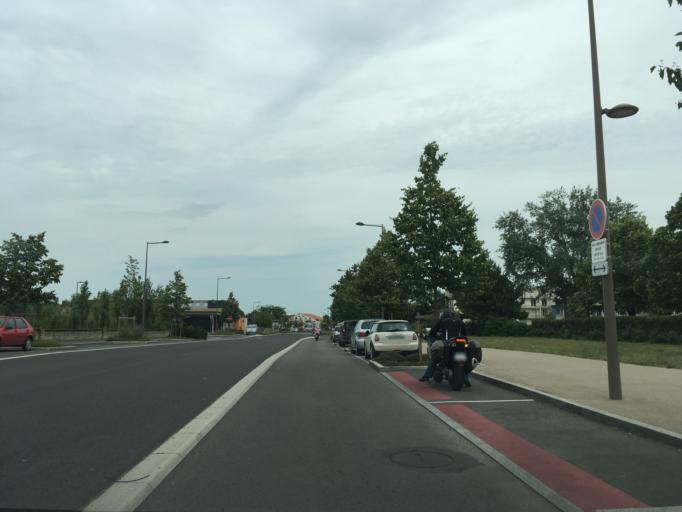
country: FR
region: Poitou-Charentes
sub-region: Departement des Deux-Sevres
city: Niort
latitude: 46.3167
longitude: -0.4795
